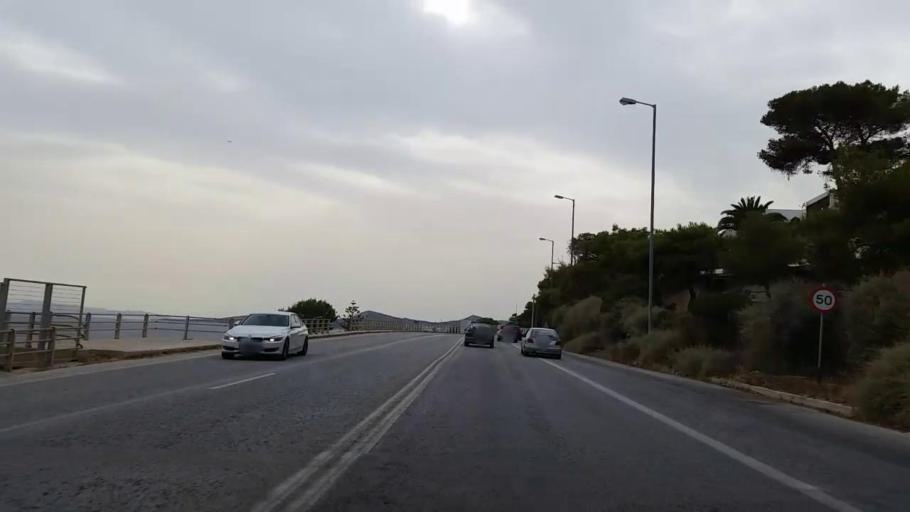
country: GR
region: Attica
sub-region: Nomarchia Anatolikis Attikis
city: Agios Dimitrios Kropias
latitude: 37.8045
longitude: 23.8555
